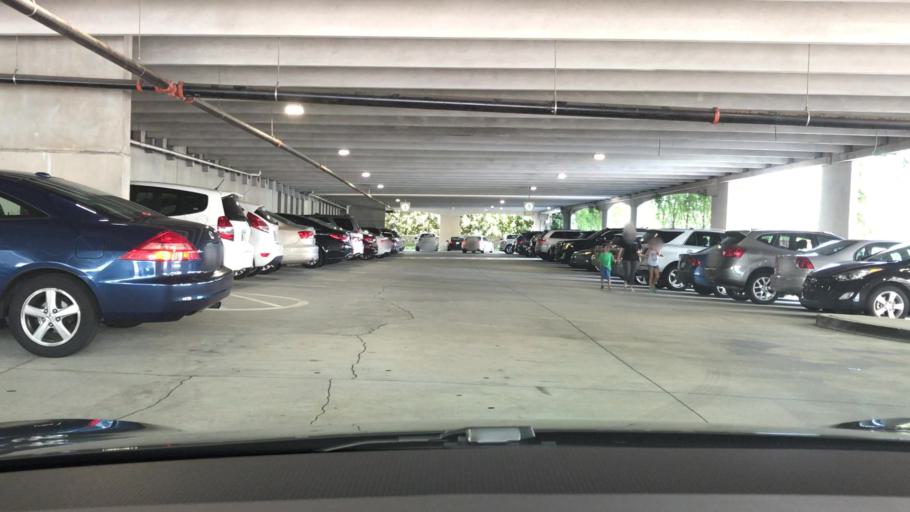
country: US
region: Georgia
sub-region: Fulton County
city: Alpharetta
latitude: 34.0715
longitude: -84.2750
